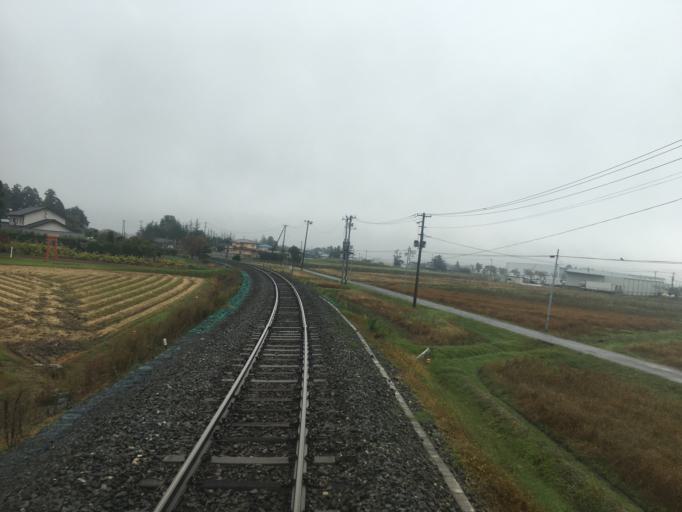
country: JP
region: Miyagi
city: Furukawa
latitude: 38.5755
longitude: 140.8981
